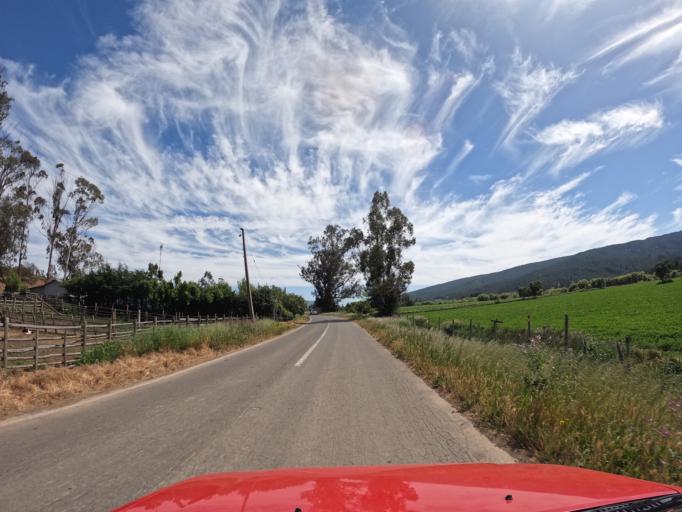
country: CL
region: Maule
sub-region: Provincia de Talca
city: Constitucion
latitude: -35.0065
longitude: -72.0313
